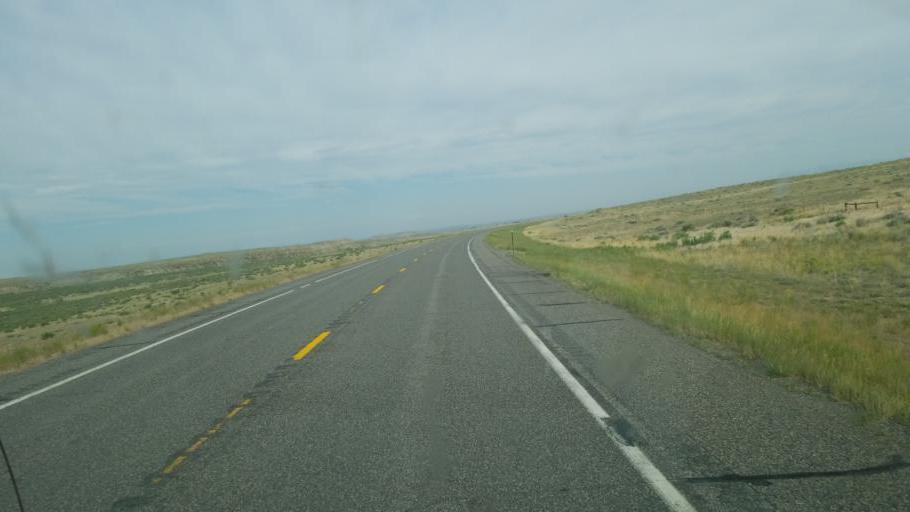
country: US
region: Wyoming
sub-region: Fremont County
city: Riverton
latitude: 43.2237
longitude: -108.0426
